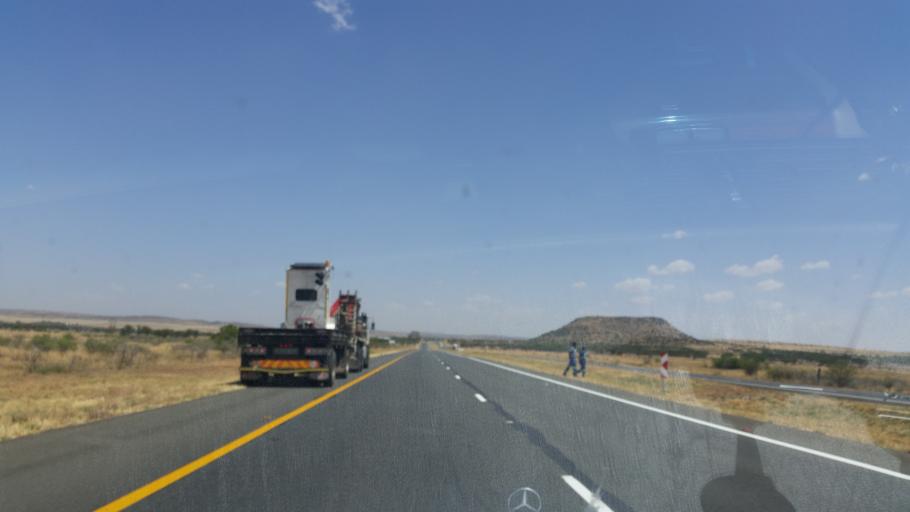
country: ZA
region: Orange Free State
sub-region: Lejweleputswa District Municipality
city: Brandfort
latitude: -28.9439
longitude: 26.4058
